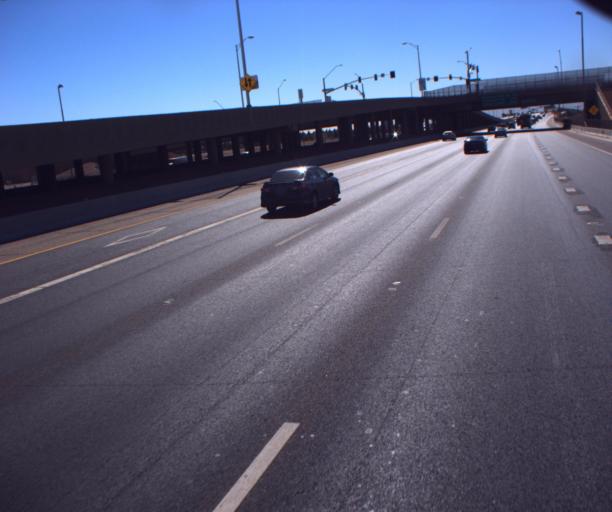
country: US
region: Arizona
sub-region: Maricopa County
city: Peoria
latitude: 33.5314
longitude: -112.2696
